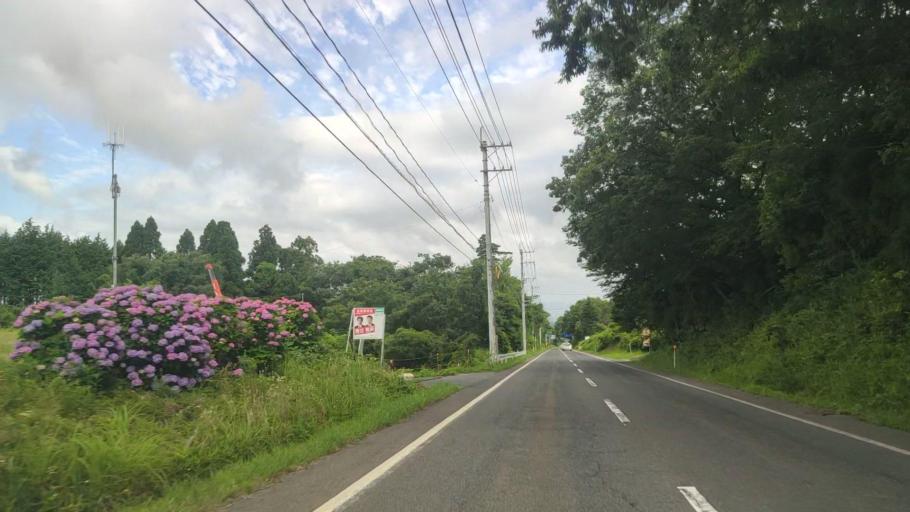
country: JP
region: Tottori
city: Yonago
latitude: 35.4105
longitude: 133.4744
